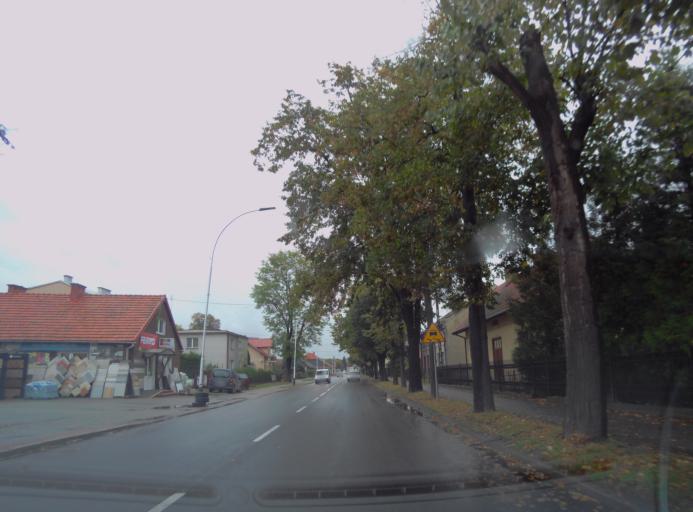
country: PL
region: Subcarpathian Voivodeship
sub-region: Powiat lezajski
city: Lezajsk
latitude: 50.2655
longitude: 22.4134
